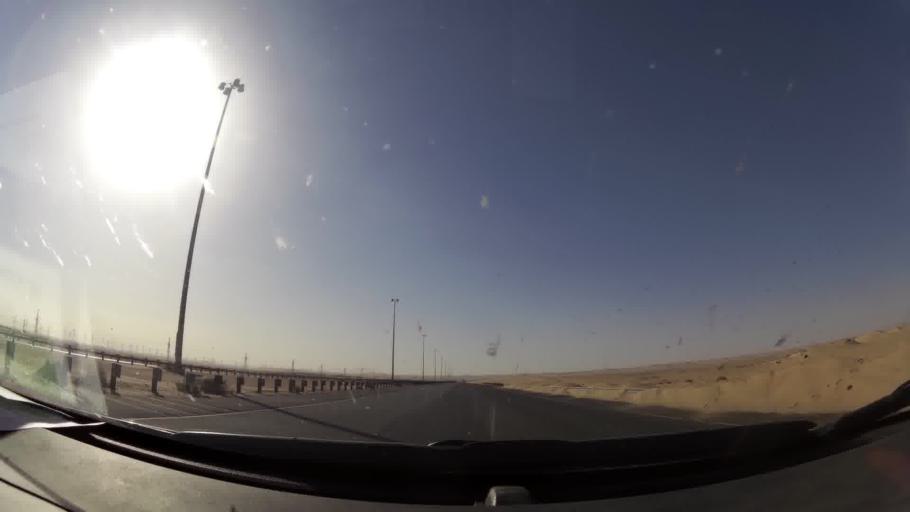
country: KW
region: Al Asimah
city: Kuwait City
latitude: 29.6457
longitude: 47.9568
